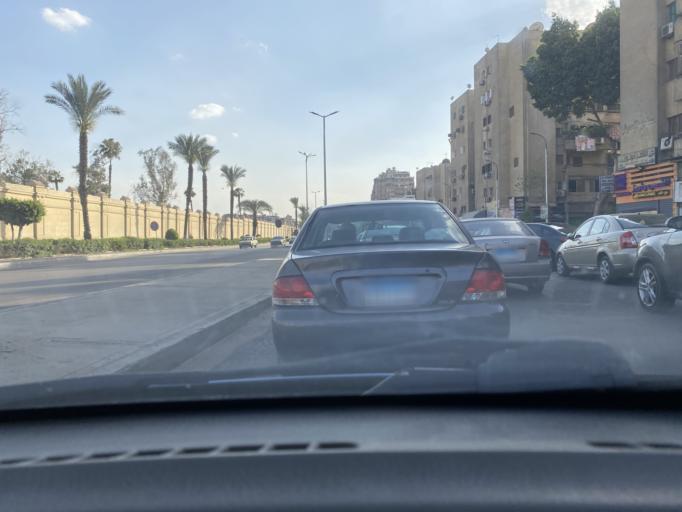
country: EG
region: Muhafazat al Qahirah
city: Cairo
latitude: 30.0932
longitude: 31.2943
